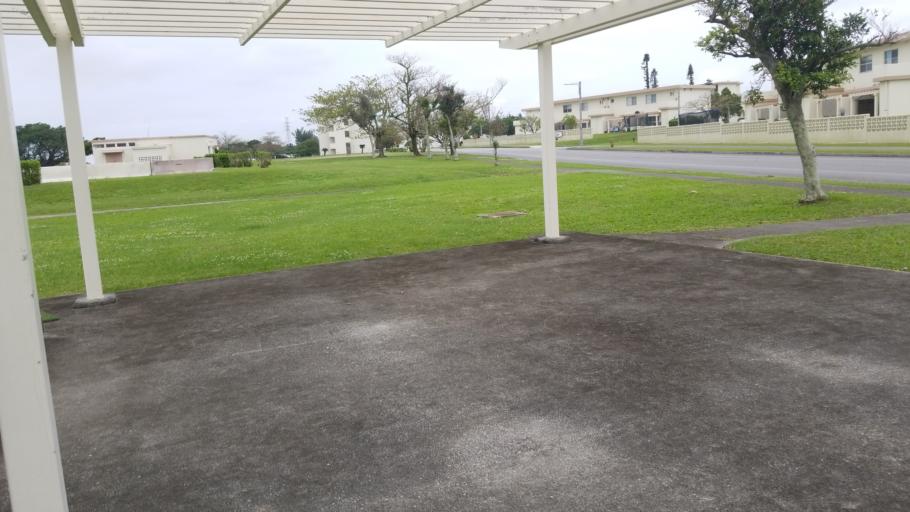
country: JP
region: Okinawa
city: Okinawa
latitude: 26.3367
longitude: 127.7758
